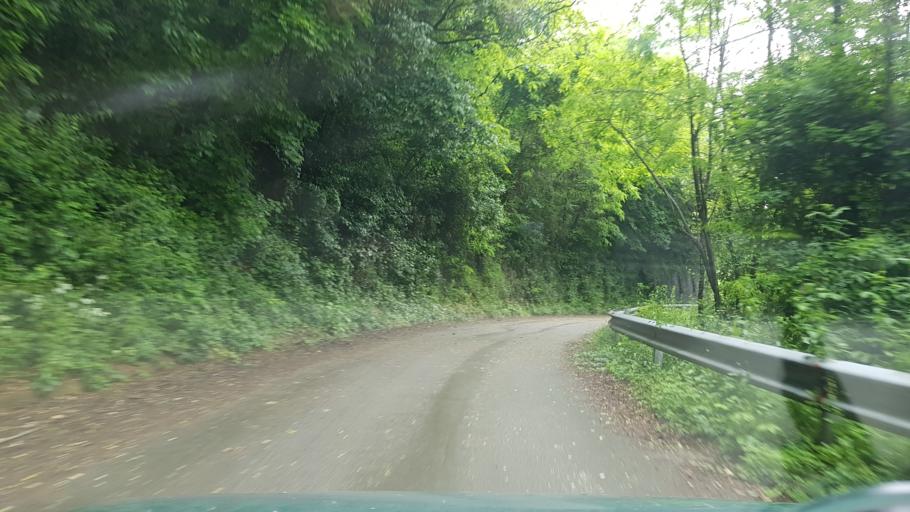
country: IT
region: Friuli Venezia Giulia
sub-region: Provincia di Gorizia
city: Gorizia
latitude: 45.9477
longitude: 13.5905
